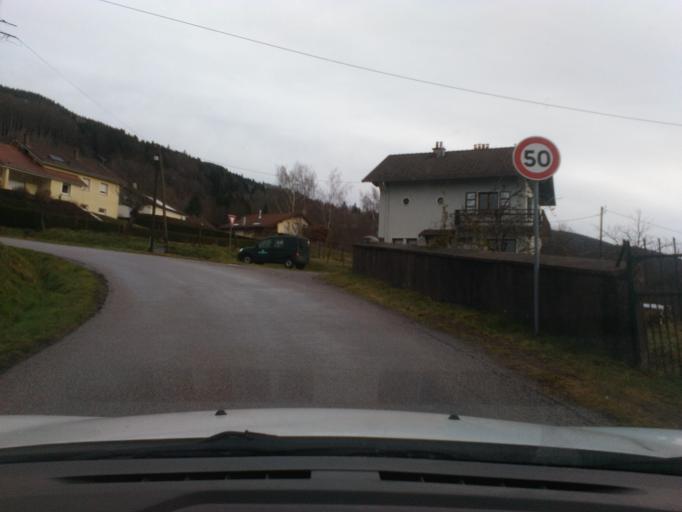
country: FR
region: Lorraine
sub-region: Departement des Vosges
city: Cornimont
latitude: 47.9672
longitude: 6.8544
